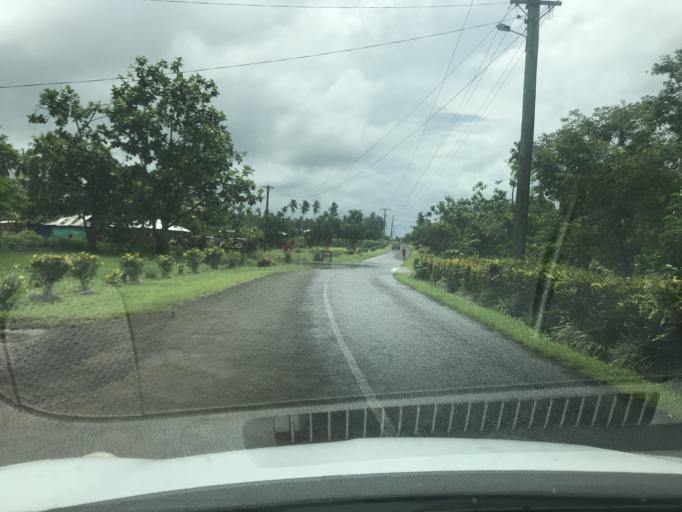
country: WS
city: Matavai
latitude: -14.0321
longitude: -171.6364
